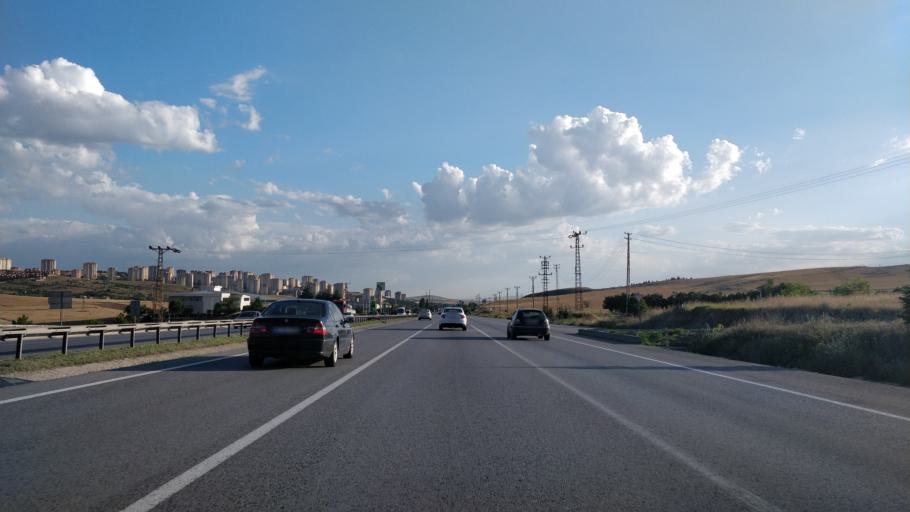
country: TR
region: Ankara
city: Etimesgut
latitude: 39.8360
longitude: 32.5853
